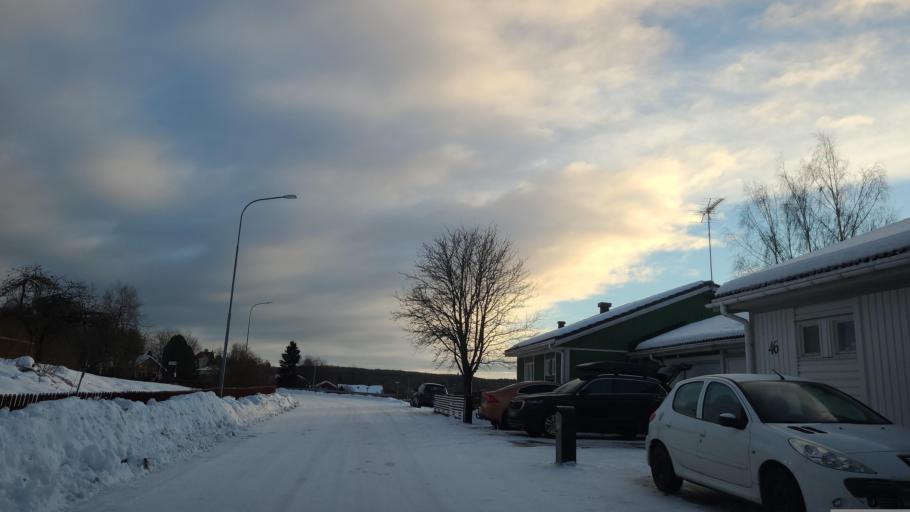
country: SE
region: Gaevleborg
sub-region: Bollnas Kommun
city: Bollnas
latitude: 61.3593
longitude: 16.4184
